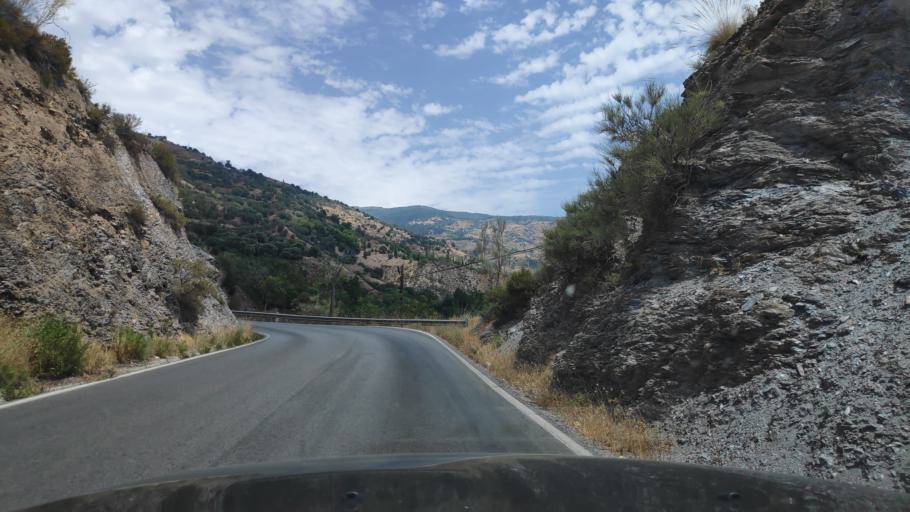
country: ES
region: Andalusia
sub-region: Provincia de Granada
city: Canar
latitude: 36.9152
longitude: -3.4278
